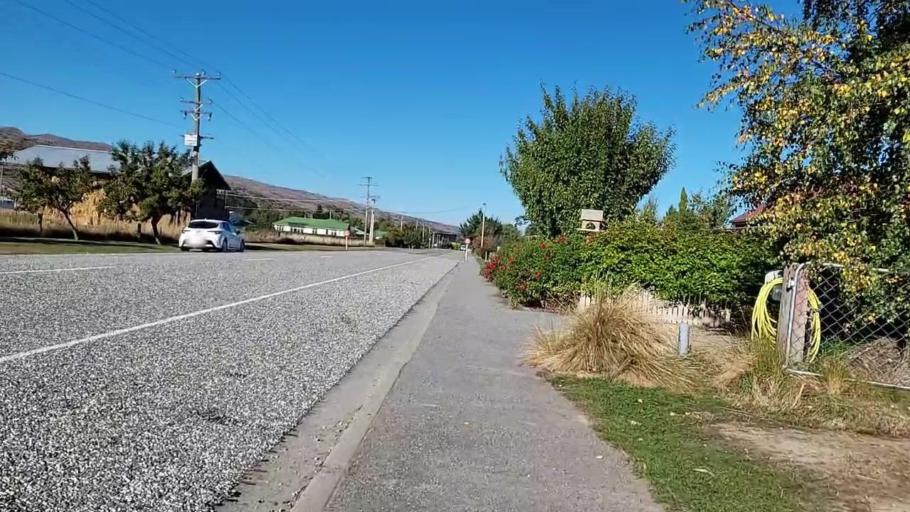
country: NZ
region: Otago
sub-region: Queenstown-Lakes District
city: Wanaka
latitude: -45.0045
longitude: 169.9154
